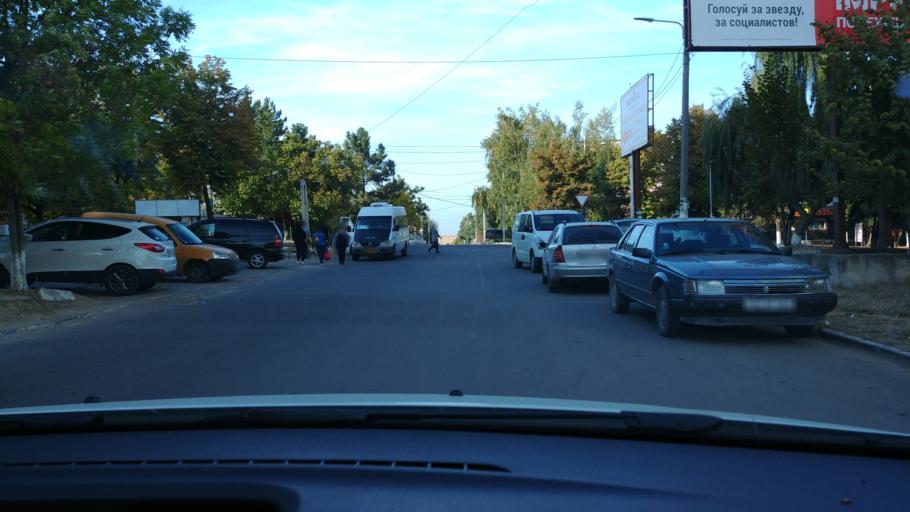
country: MD
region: Rezina
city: Rezina
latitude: 47.7484
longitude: 28.9561
